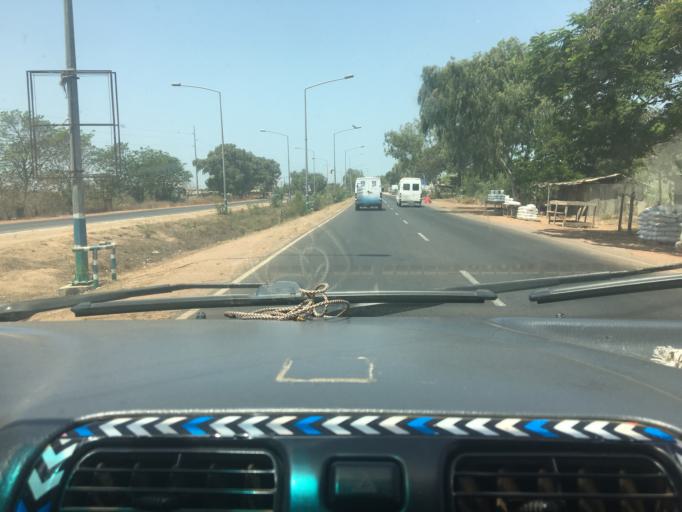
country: GM
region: Banjul
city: Bakau
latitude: 13.4686
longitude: -16.6323
